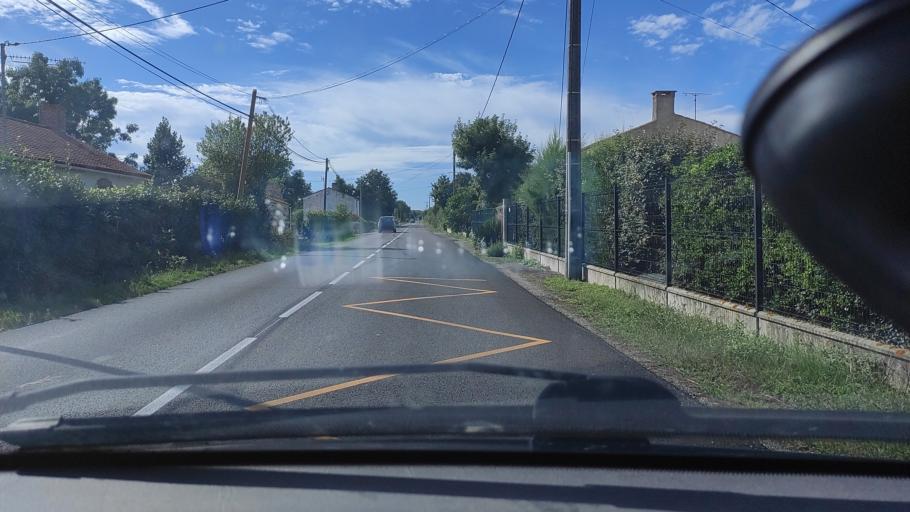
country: FR
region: Pays de la Loire
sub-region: Departement de la Vendee
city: La Boissiere-des-Landes
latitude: 46.5557
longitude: -1.4368
